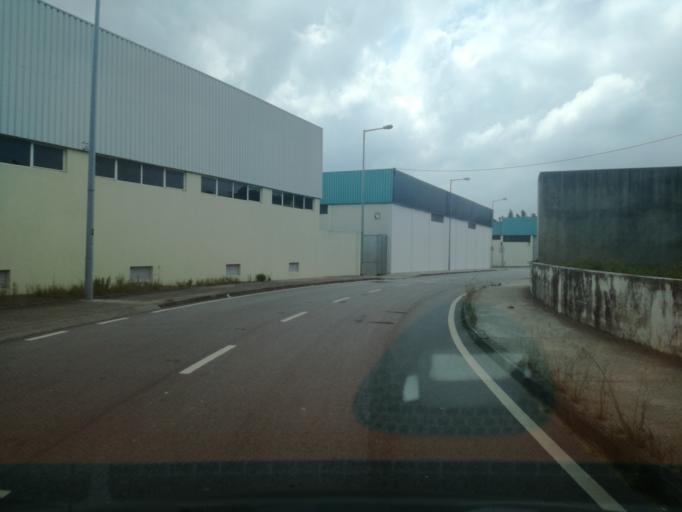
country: PT
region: Porto
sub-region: Maia
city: Anta
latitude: 41.2592
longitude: -8.6335
